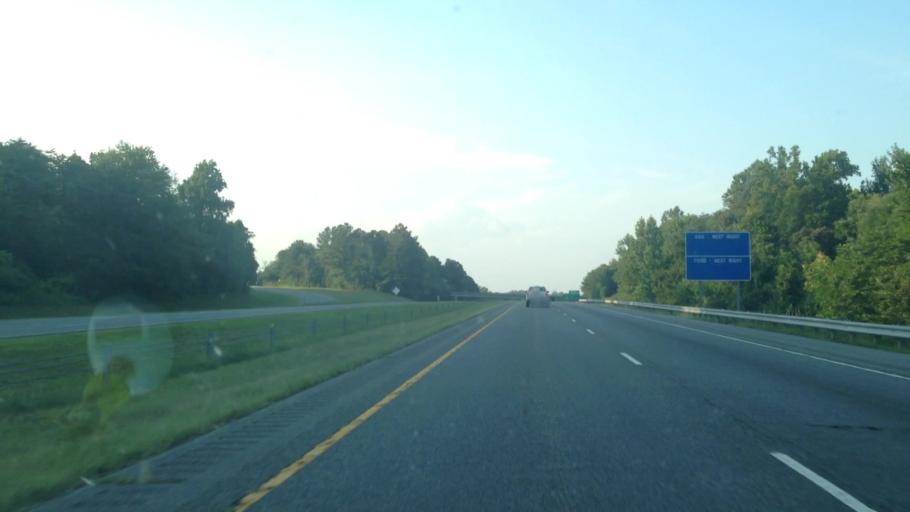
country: US
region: North Carolina
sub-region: Rockingham County
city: Reidsville
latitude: 36.3972
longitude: -79.5988
